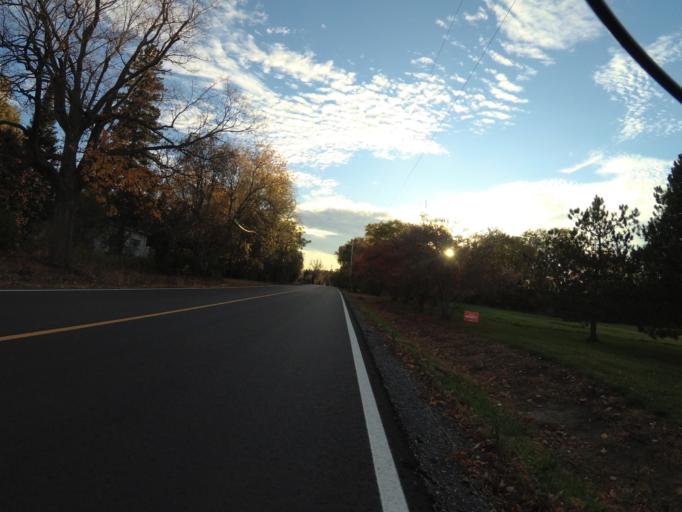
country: CA
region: Ontario
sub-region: Lanark County
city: Smiths Falls
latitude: 44.9614
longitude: -75.8116
